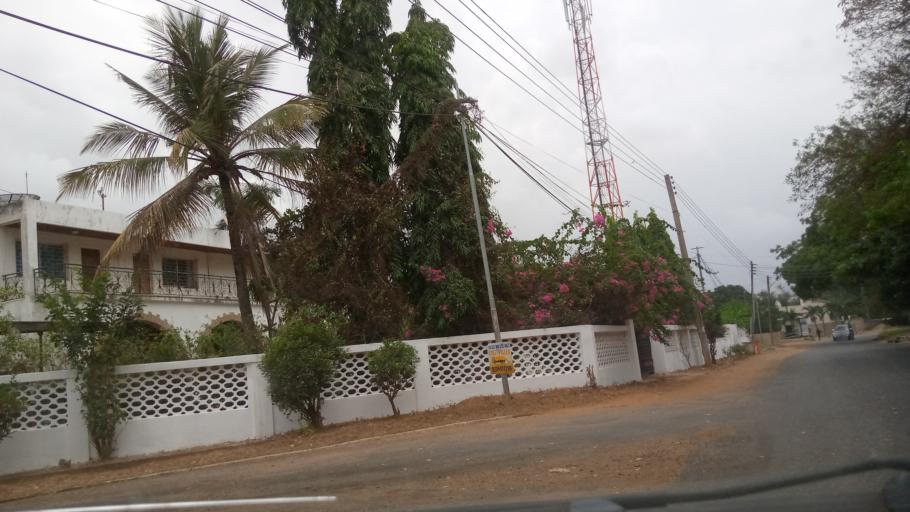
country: GH
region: Greater Accra
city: Accra
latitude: 5.6097
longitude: -0.1852
